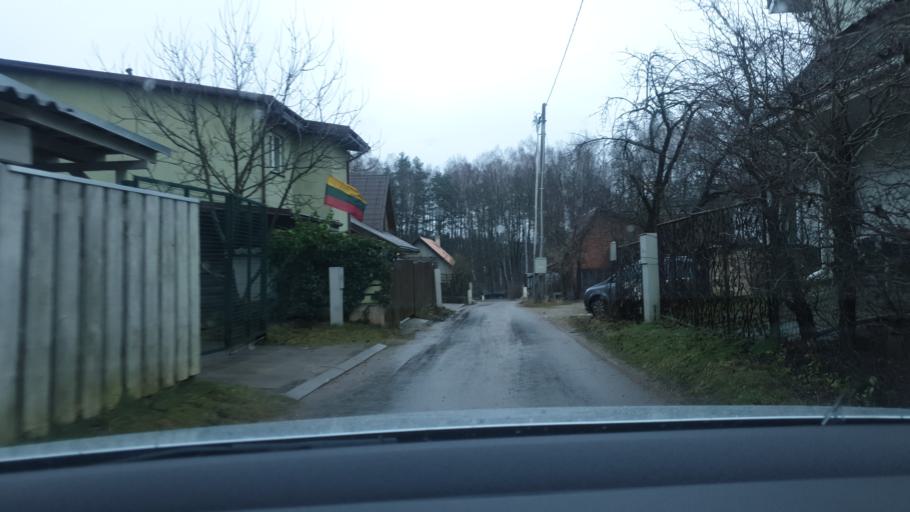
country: LT
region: Vilnius County
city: Rasos
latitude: 54.7179
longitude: 25.3817
